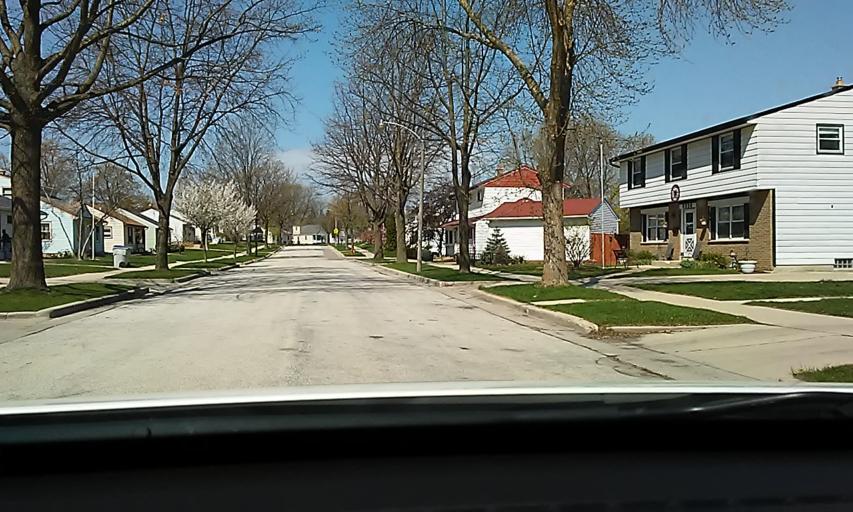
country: US
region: Wisconsin
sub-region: Milwaukee County
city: West Milwaukee
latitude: 42.9901
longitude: -87.9907
